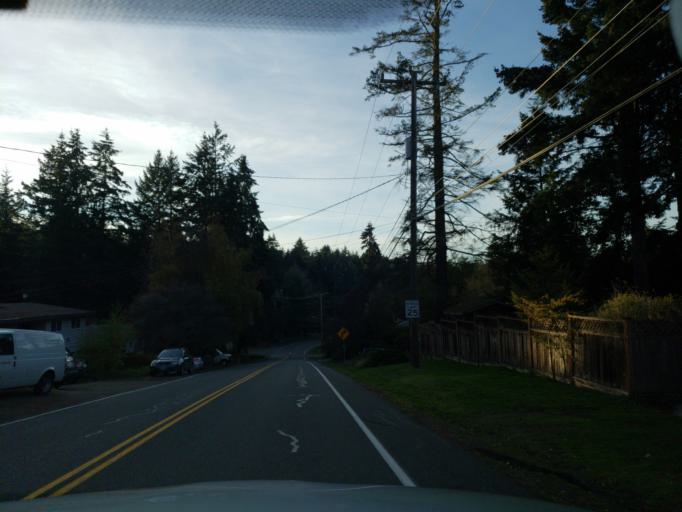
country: US
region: Washington
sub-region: King County
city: Shoreline
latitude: 47.7487
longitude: -122.3511
